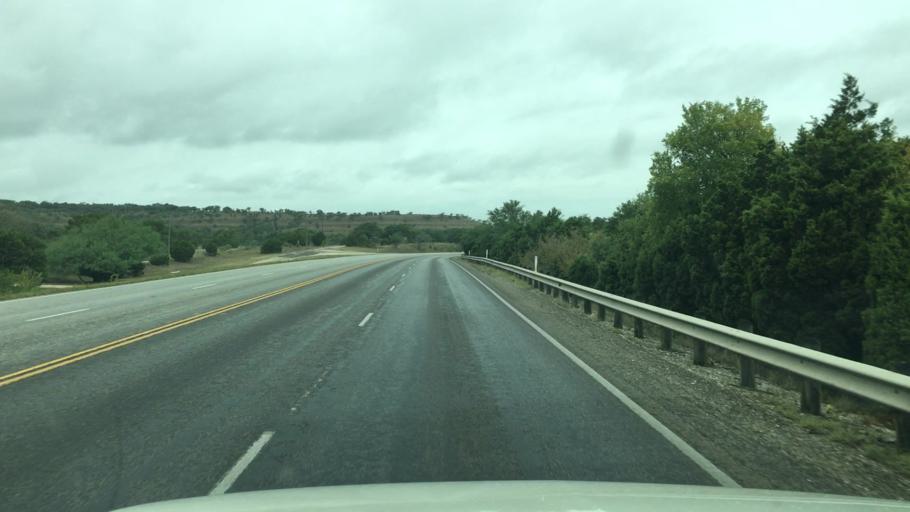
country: US
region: Texas
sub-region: Hays County
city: Dripping Springs
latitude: 30.1923
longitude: -98.2272
